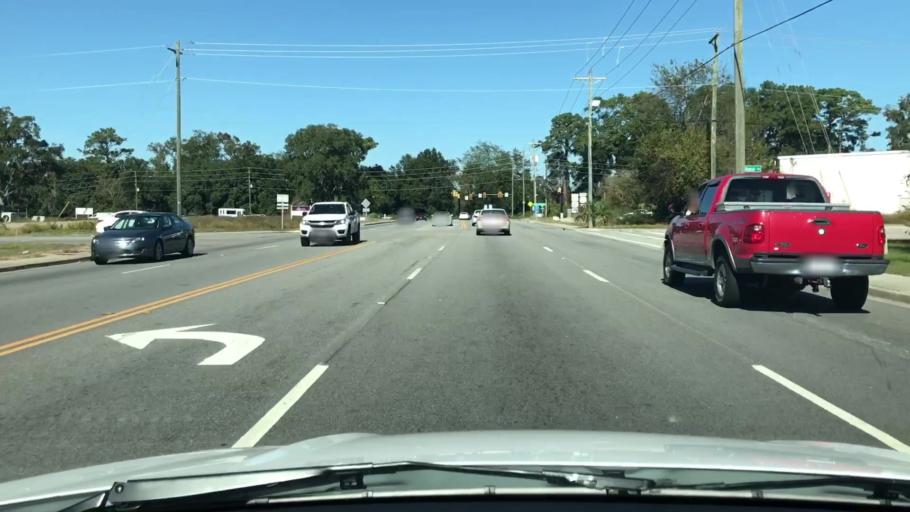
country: US
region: South Carolina
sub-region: Beaufort County
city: Burton
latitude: 32.4401
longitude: -80.7218
